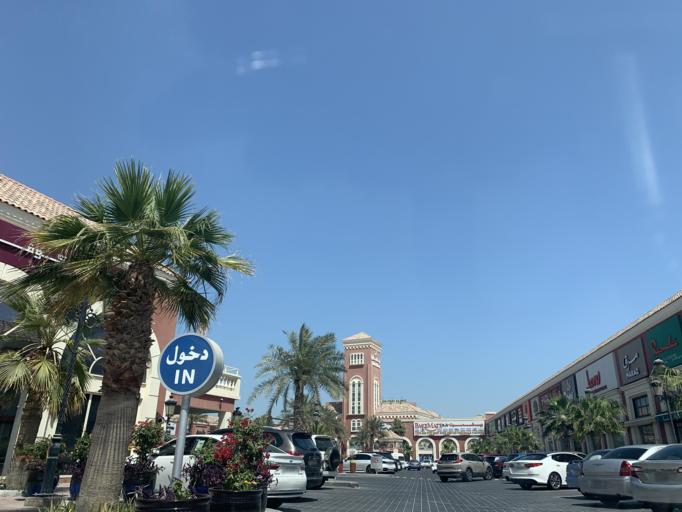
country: BH
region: Manama
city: Manama
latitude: 26.2107
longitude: 50.5719
